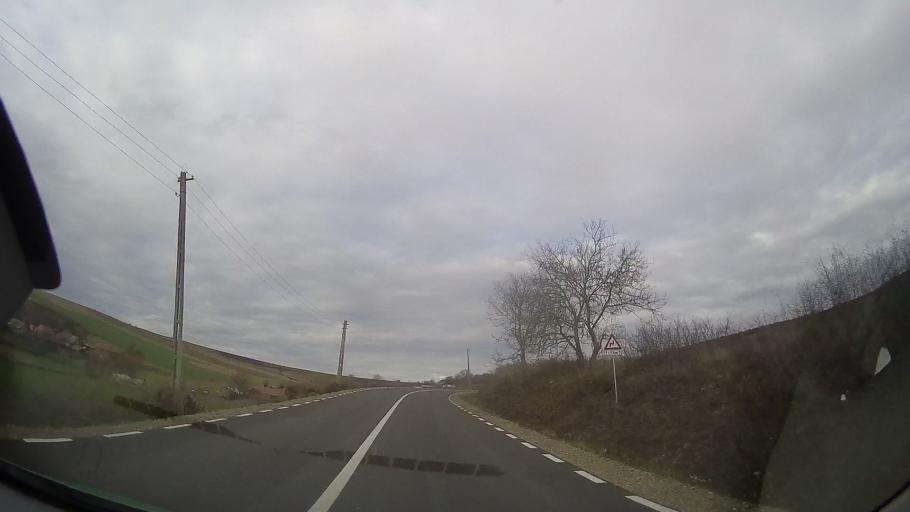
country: RO
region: Bistrita-Nasaud
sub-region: Comuna Teaca
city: Ocnita
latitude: 46.8211
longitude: 24.4842
